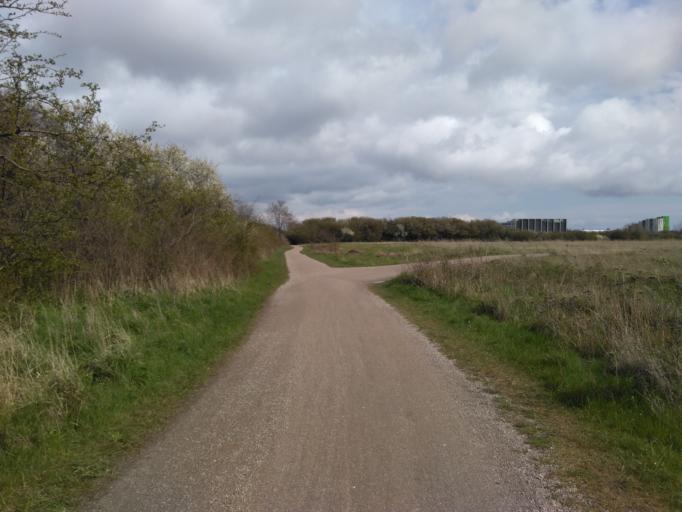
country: DK
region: Capital Region
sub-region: Tarnby Kommune
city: Tarnby
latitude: 55.6443
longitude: 12.5750
